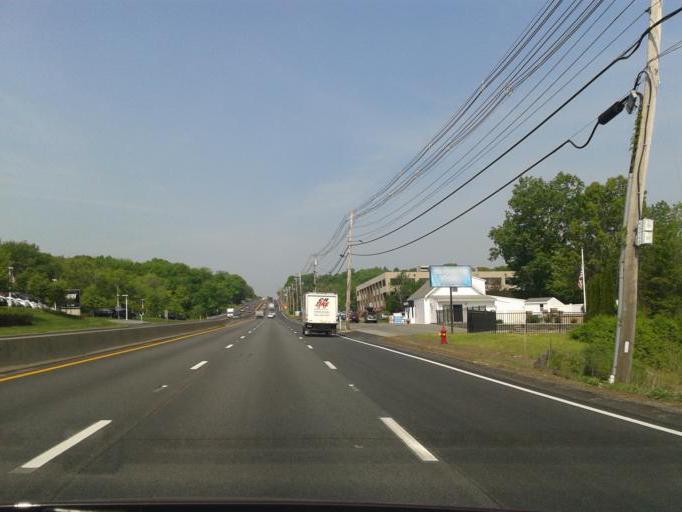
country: US
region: Massachusetts
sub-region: Worcester County
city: Southborough
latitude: 42.2912
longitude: -71.5318
